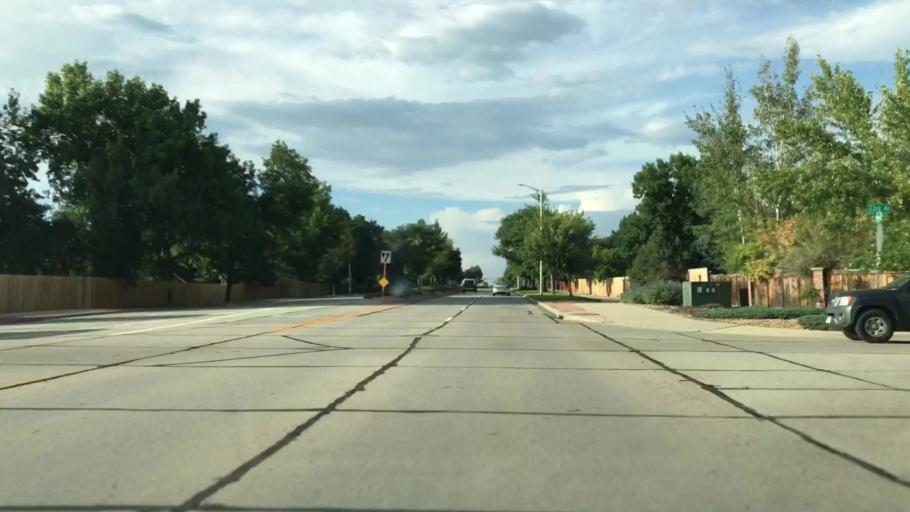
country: US
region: Colorado
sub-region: Boulder County
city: Longmont
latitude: 40.1993
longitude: -105.1309
